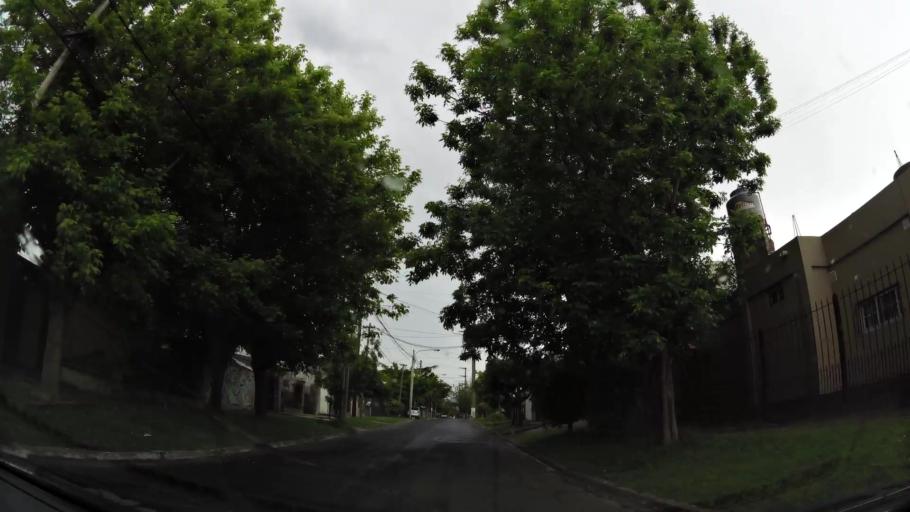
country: AR
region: Buenos Aires
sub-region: Partido de Quilmes
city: Quilmes
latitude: -34.7697
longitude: -58.2090
